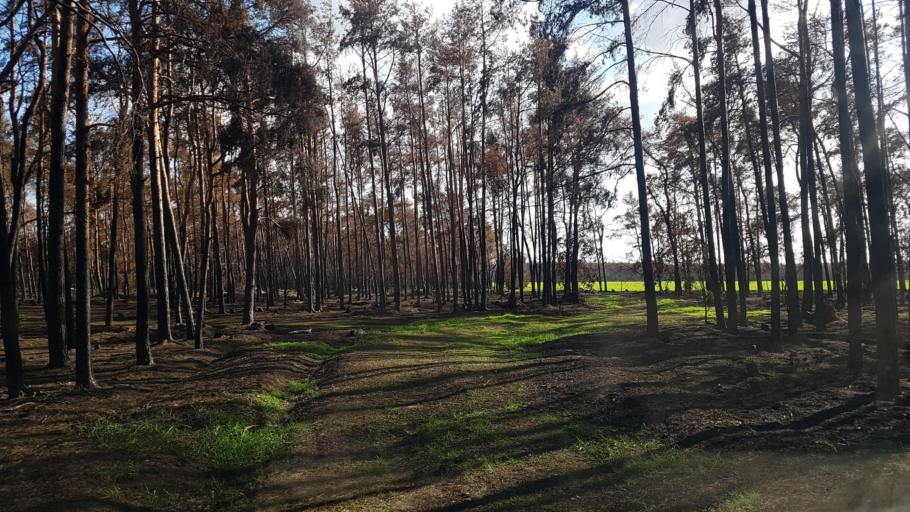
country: DE
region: Saxony
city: Nauwalde
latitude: 51.4432
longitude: 13.3313
